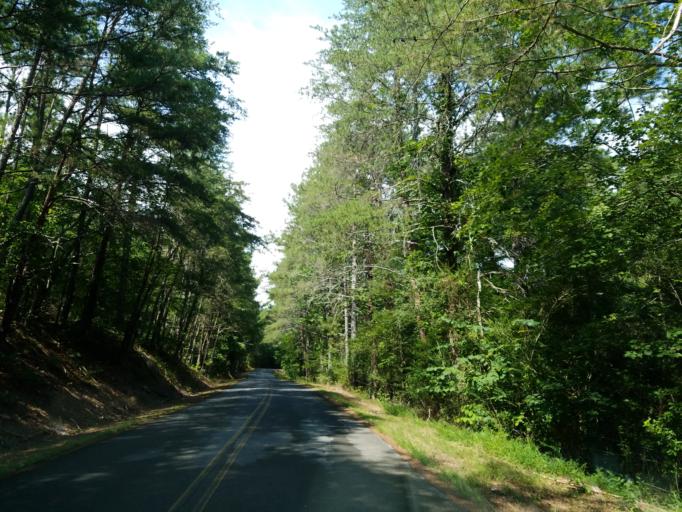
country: US
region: Georgia
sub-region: Bartow County
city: Rydal
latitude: 34.5372
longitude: -84.7217
